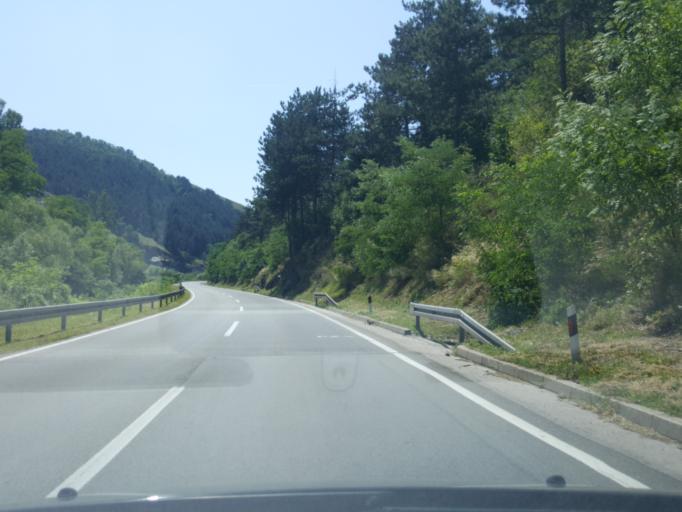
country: RS
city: Prislonica
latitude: 43.9925
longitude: 20.4215
